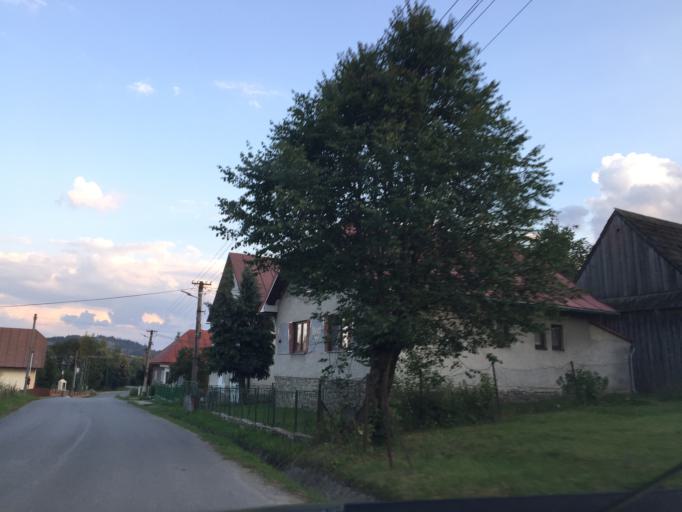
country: PL
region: Silesian Voivodeship
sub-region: Powiat zywiecki
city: Korbielow
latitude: 49.4817
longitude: 19.3812
